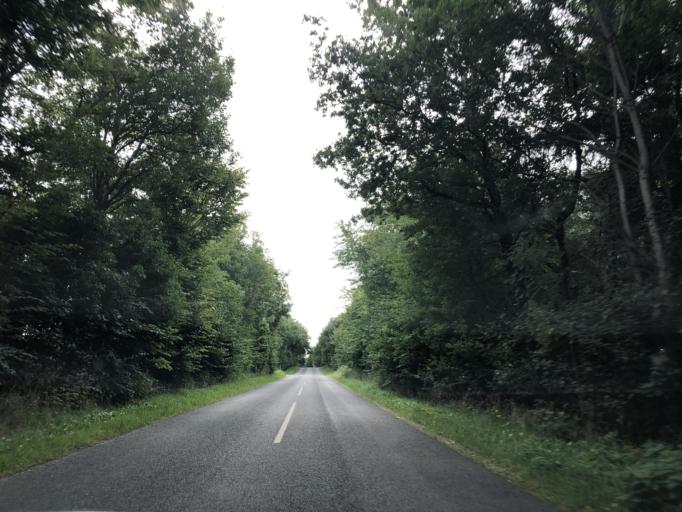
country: DK
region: North Denmark
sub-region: Vesthimmerland Kommune
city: Alestrup
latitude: 56.6019
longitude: 9.4330
